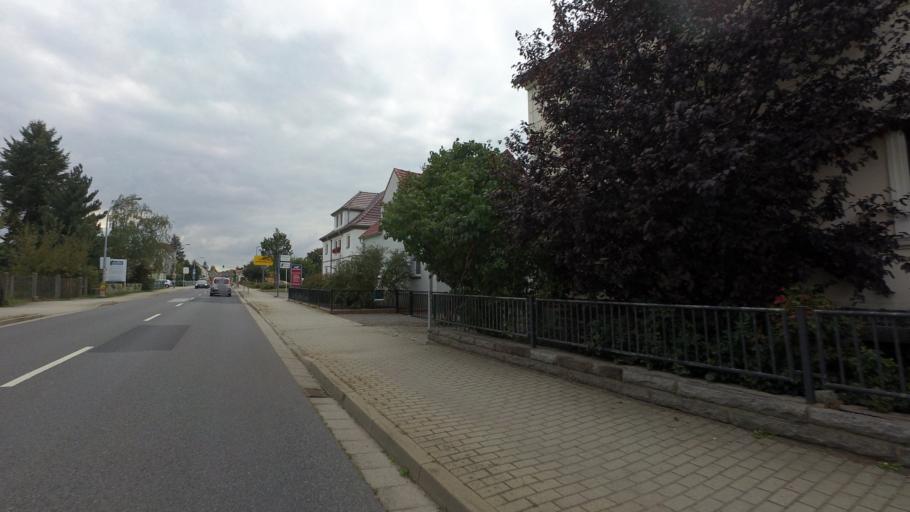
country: DE
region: Saxony
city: Konigswartha
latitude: 51.3147
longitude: 14.3320
